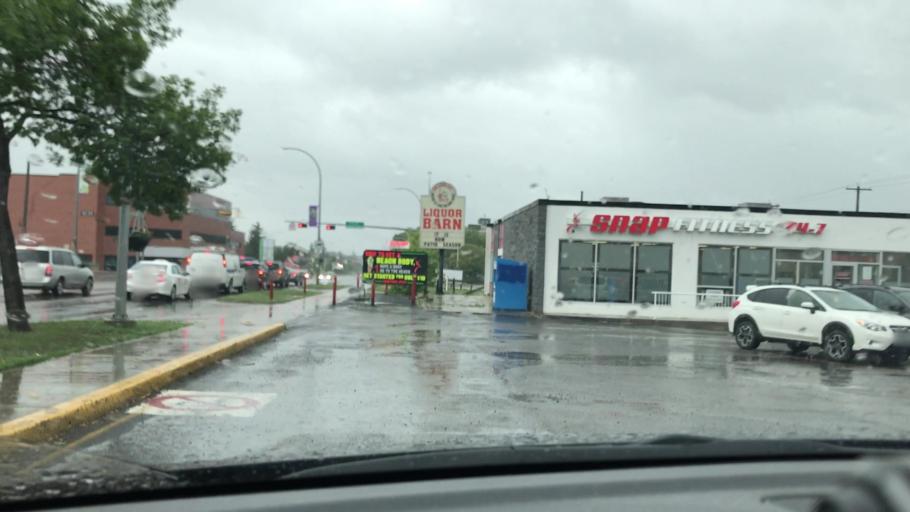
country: CA
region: Alberta
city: Edmonton
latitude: 53.5181
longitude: -113.4662
